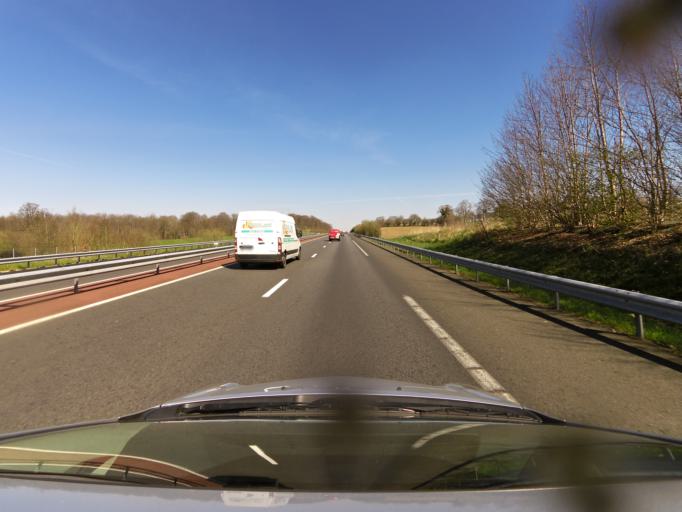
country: FR
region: Lower Normandy
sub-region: Departement de la Manche
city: Saint-Senier-sous-Avranches
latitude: 48.7615
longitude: -1.2779
